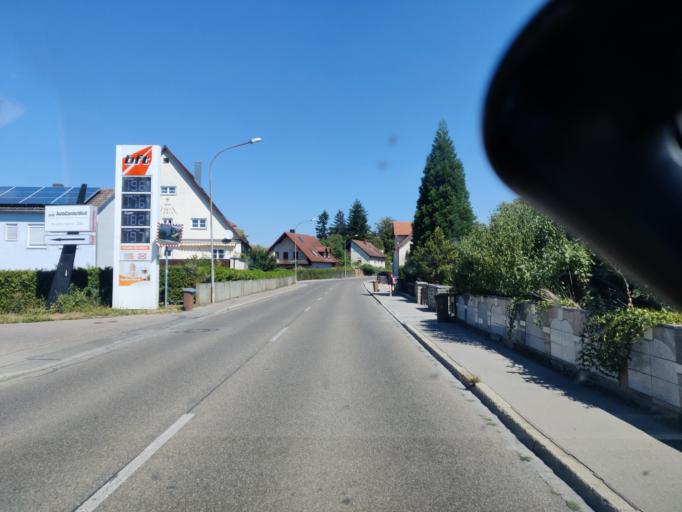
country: DE
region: Bavaria
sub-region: Regierungsbezirk Mittelfranken
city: Weissenburg in Bayern
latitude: 49.0247
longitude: 10.9671
